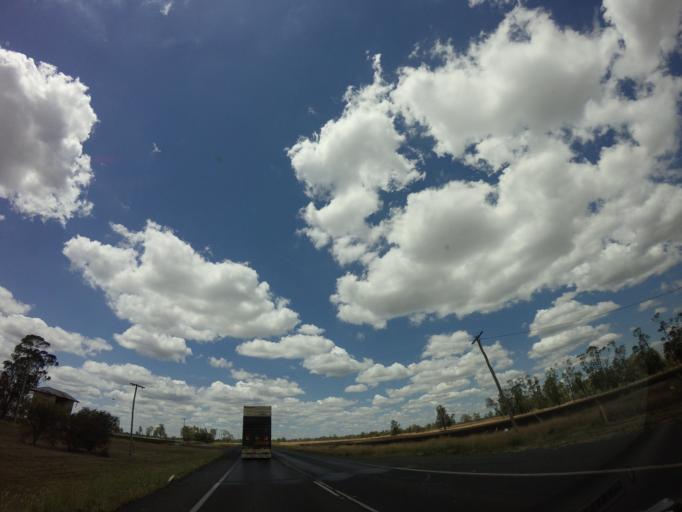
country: AU
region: Queensland
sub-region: Toowoomba
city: Oakey
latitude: -27.8274
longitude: 151.3513
